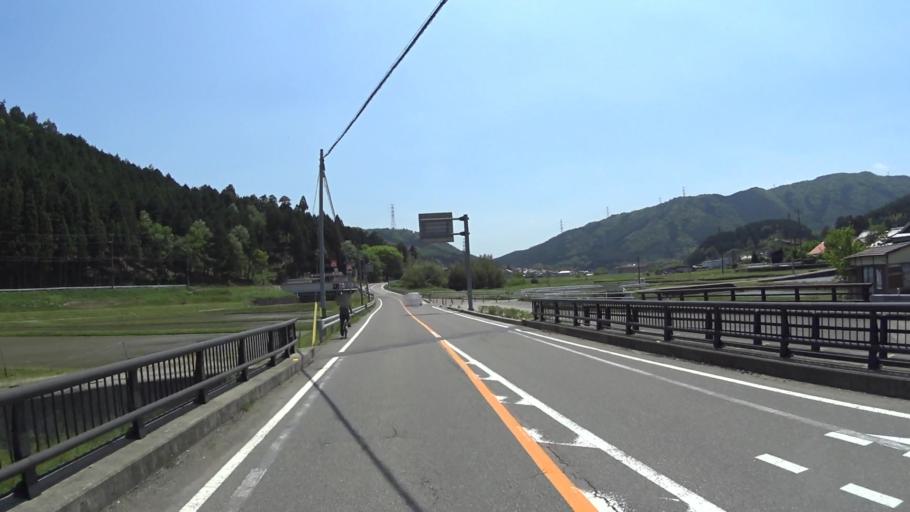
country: JP
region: Kyoto
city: Kameoka
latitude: 35.0130
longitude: 135.4868
